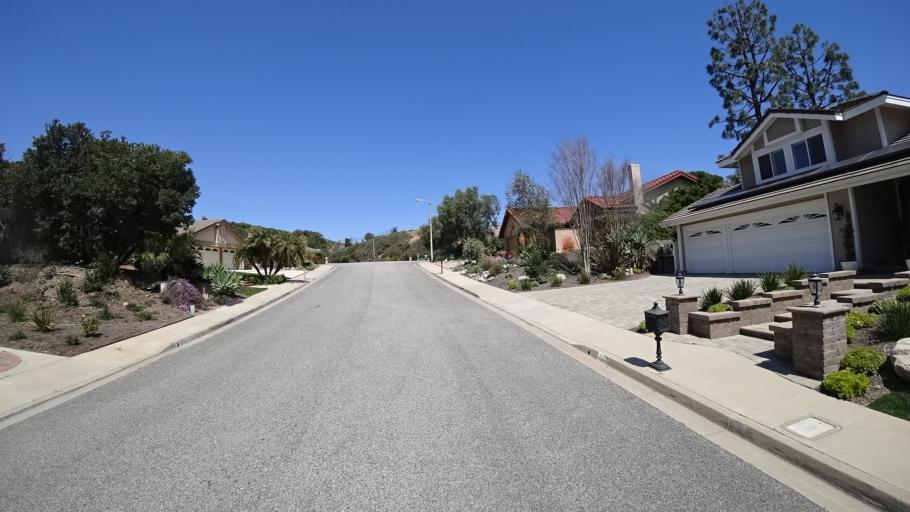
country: US
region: California
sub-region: Ventura County
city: Casa Conejo
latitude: 34.2063
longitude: -118.8903
